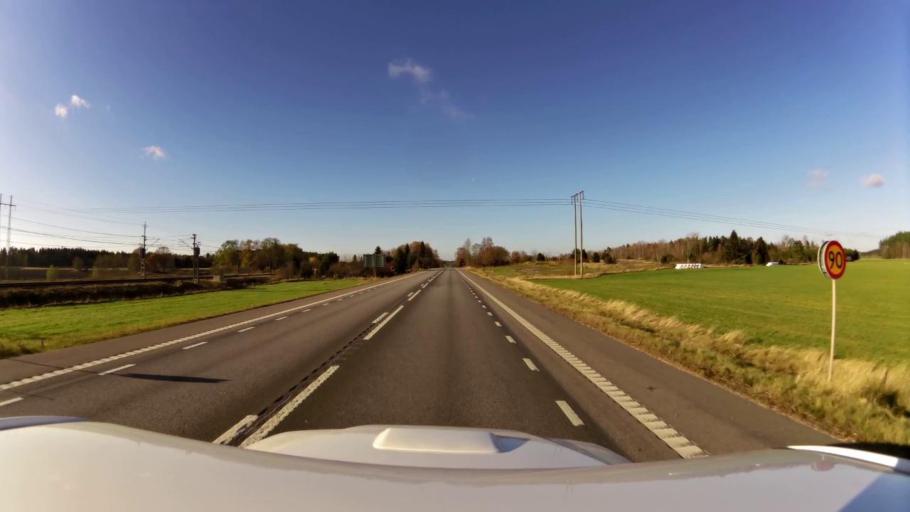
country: SE
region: OEstergoetland
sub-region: Linkopings Kommun
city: Linghem
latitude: 58.4364
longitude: 15.7723
